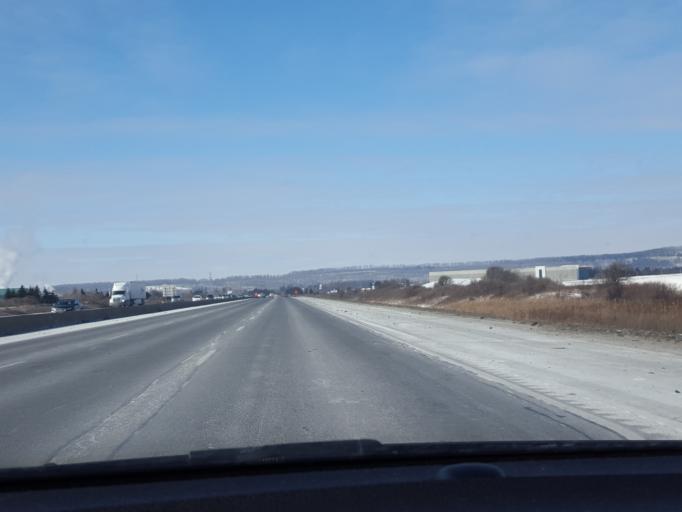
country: CA
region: Ontario
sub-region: Halton
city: Milton
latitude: 43.5261
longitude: -79.9145
